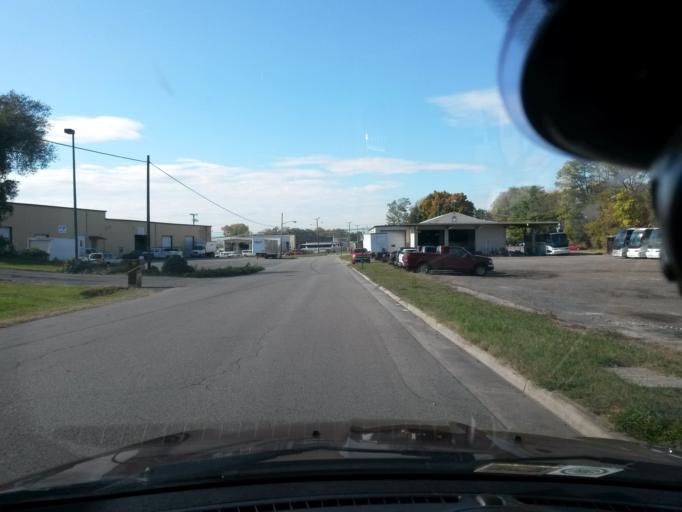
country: US
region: Virginia
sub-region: Roanoke County
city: Vinton
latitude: 37.3023
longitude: -79.9010
